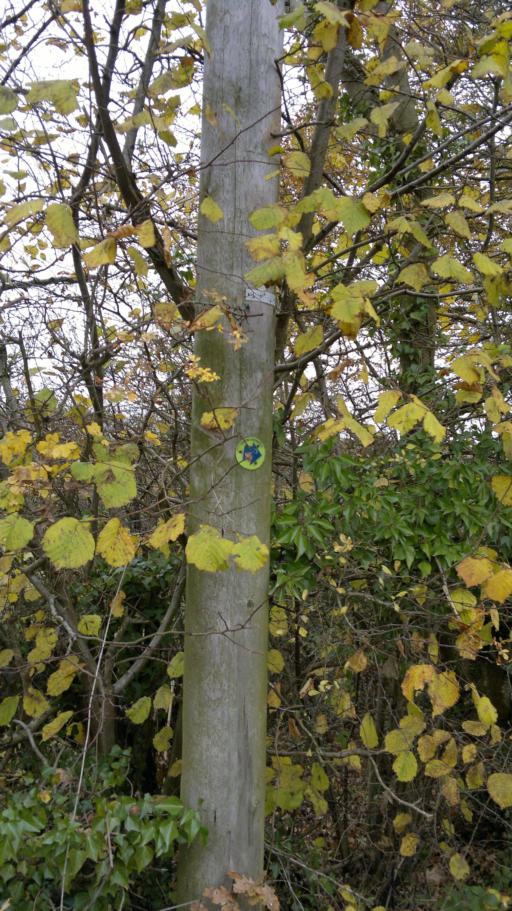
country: GB
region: England
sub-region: West Berkshire
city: Stratfield Mortimer
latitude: 51.3601
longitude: -1.0802
